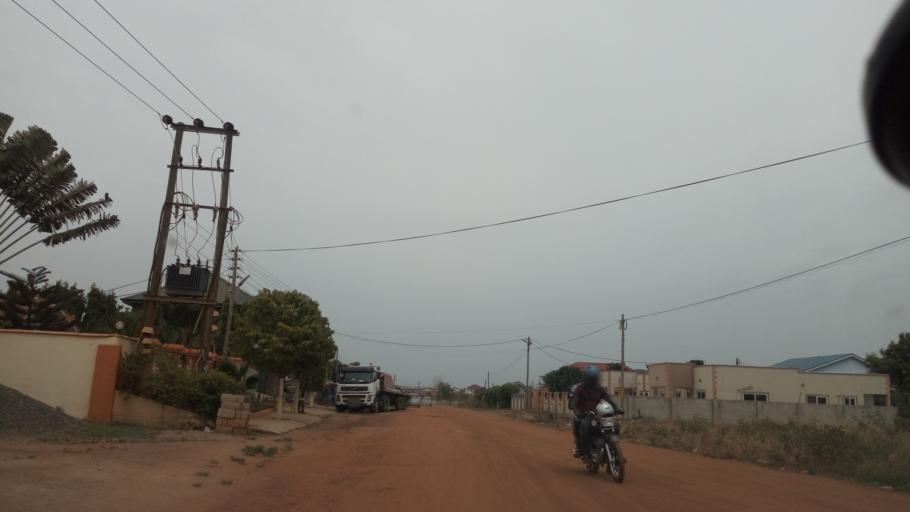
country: GH
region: Greater Accra
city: Medina Estates
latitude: 5.7027
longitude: -0.1347
